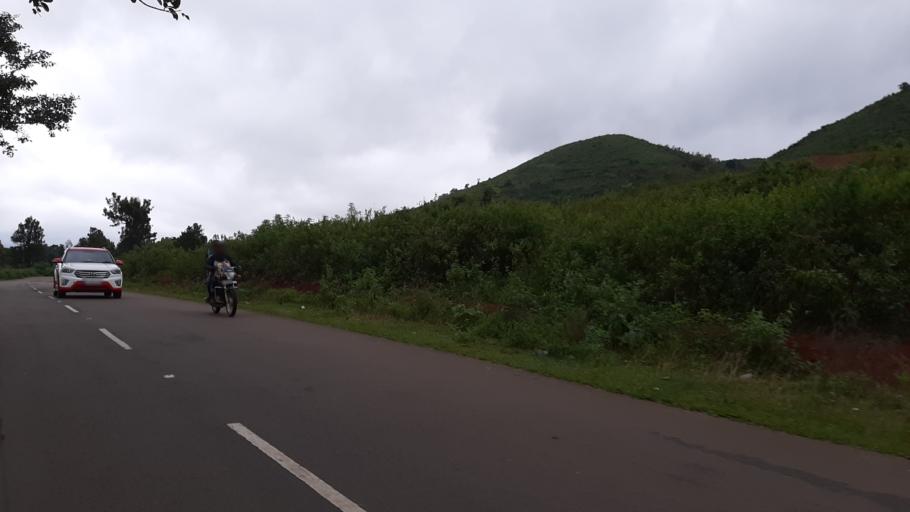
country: IN
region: Andhra Pradesh
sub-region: Vizianagaram District
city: Salur
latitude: 18.2893
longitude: 82.9265
